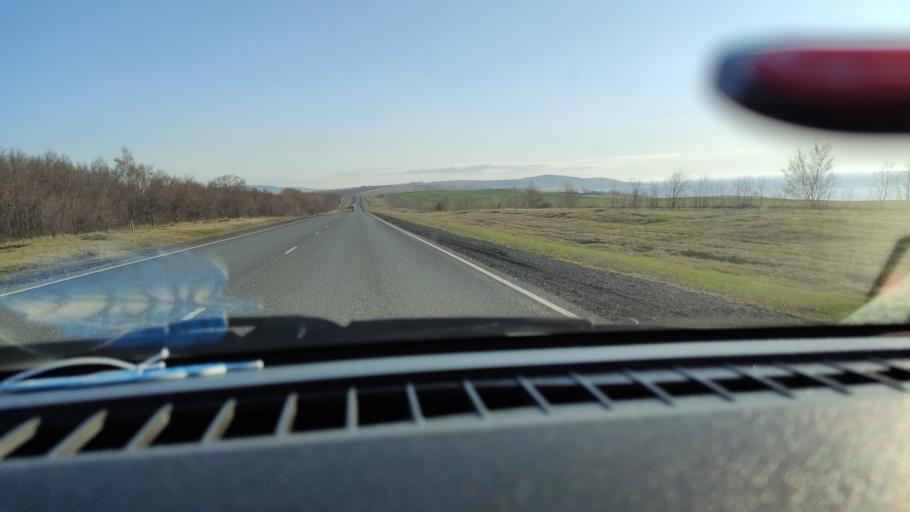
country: RU
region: Saratov
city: Balakovo
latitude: 52.1840
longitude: 47.8453
